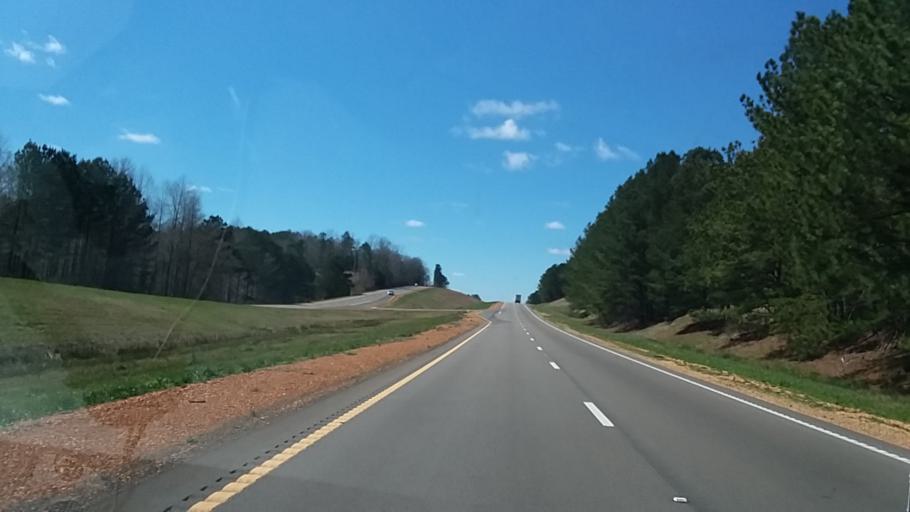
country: US
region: Mississippi
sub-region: Alcorn County
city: Farmington
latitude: 34.8536
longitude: -88.3586
